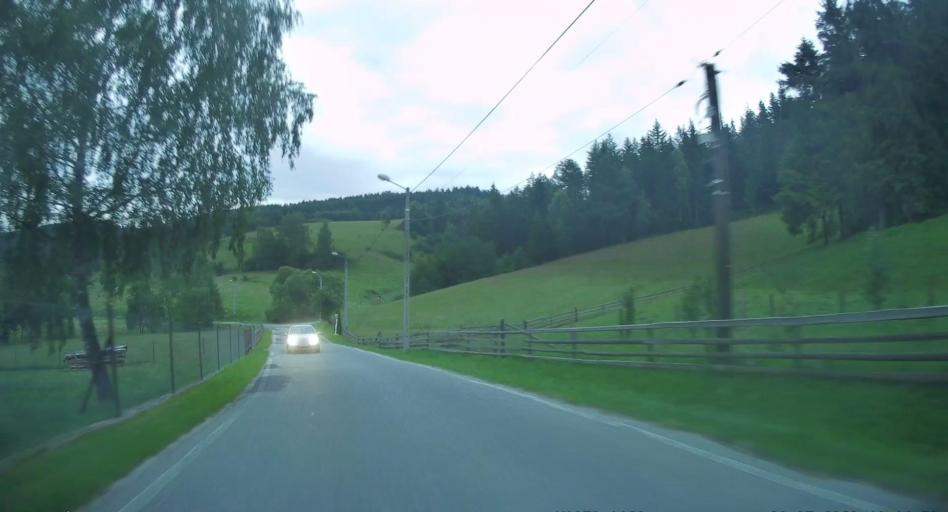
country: PL
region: Lesser Poland Voivodeship
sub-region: Powiat nowosadecki
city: Muszyna
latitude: 49.3761
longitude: 20.9238
